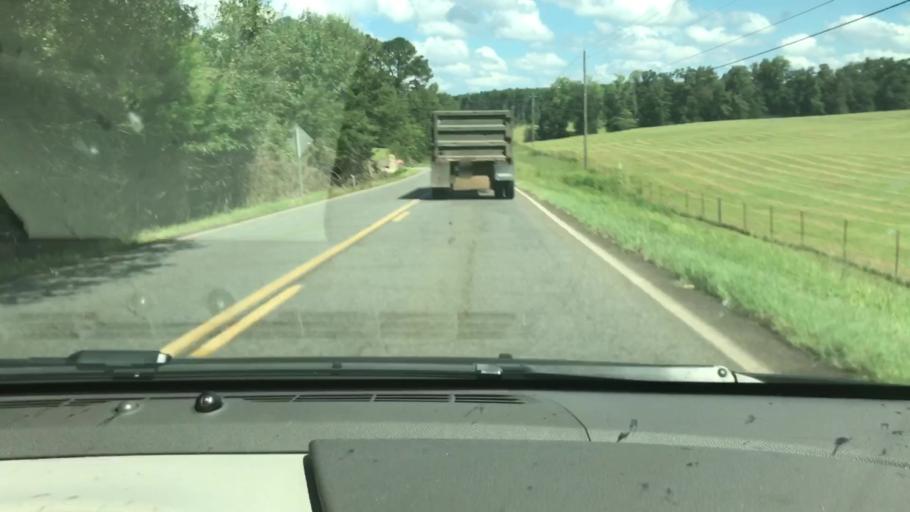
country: US
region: Alabama
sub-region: Chambers County
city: Valley
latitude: 32.8317
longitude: -85.0351
